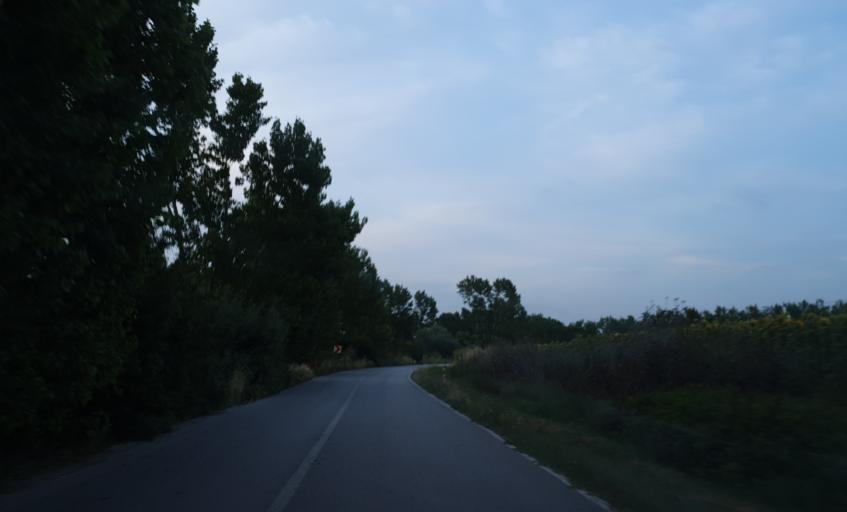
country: TR
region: Tekirdag
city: Beyazkoy
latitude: 41.3718
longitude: 27.6102
